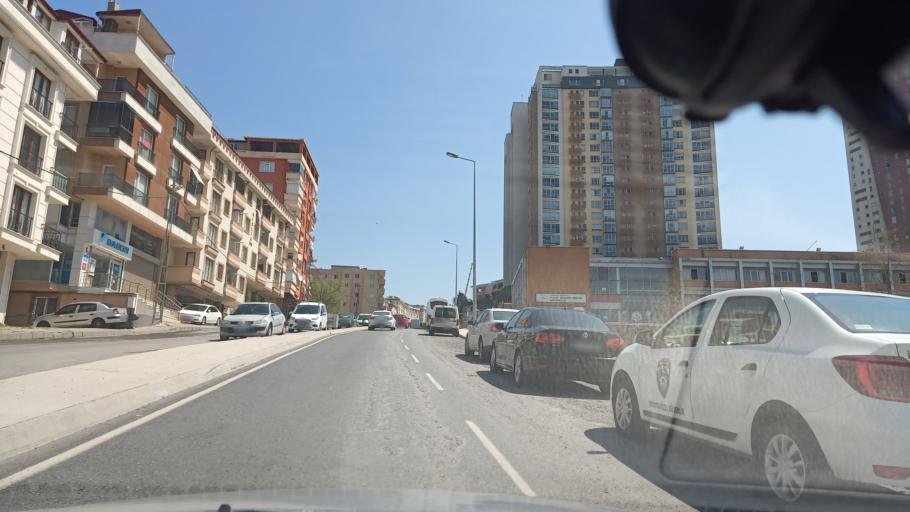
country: TR
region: Istanbul
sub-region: Atasehir
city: Atasehir
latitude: 40.9683
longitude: 29.1235
